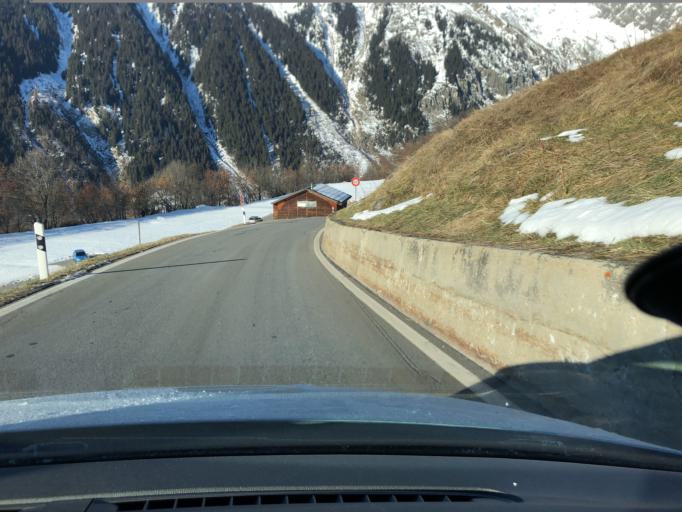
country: CH
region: Valais
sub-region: Goms District
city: Fiesch
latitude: 46.4281
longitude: 8.1516
